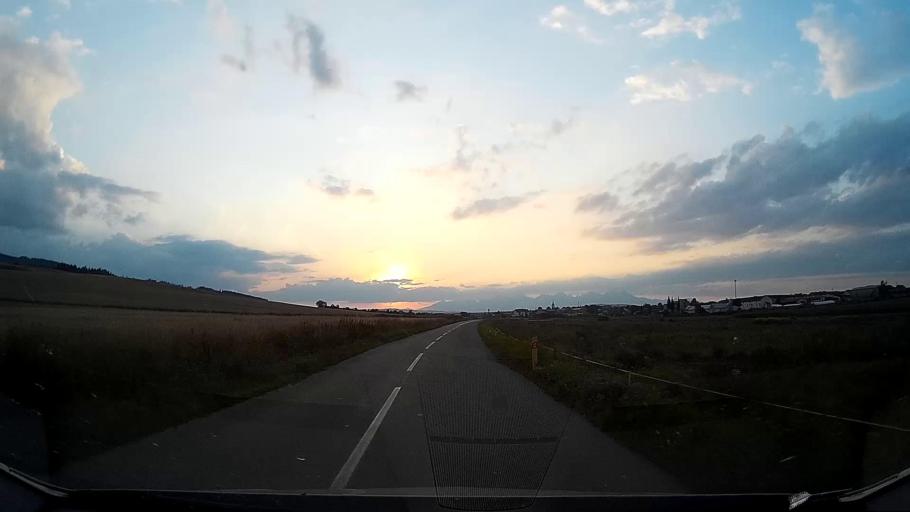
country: SK
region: Kosicky
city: Spisska Nova Ves
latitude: 48.9556
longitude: 20.4774
